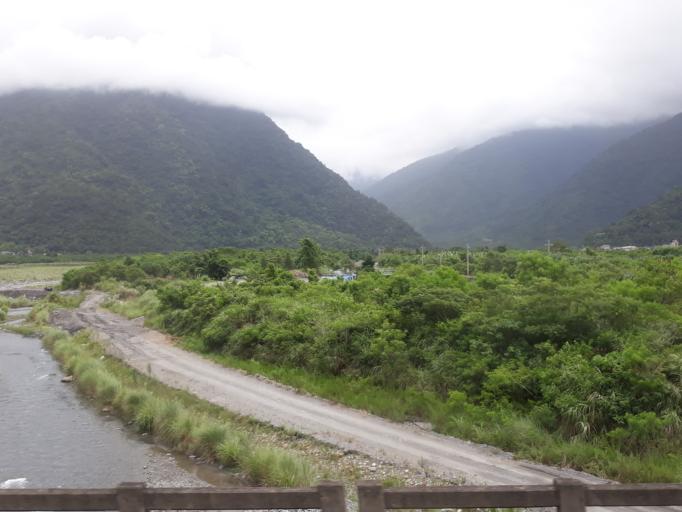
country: TW
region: Taiwan
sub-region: Yilan
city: Yilan
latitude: 24.4626
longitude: 121.7854
